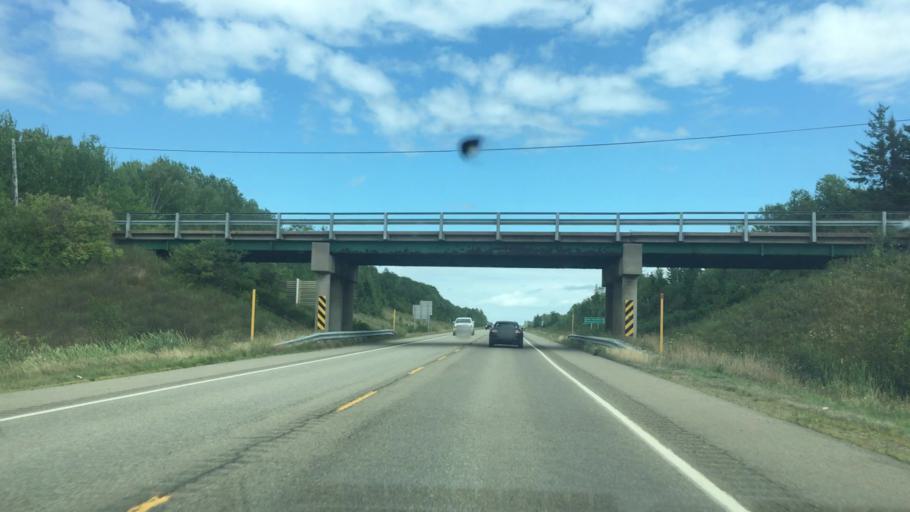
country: CA
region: Nova Scotia
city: Port Hawkesbury
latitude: 45.6194
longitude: -61.6137
